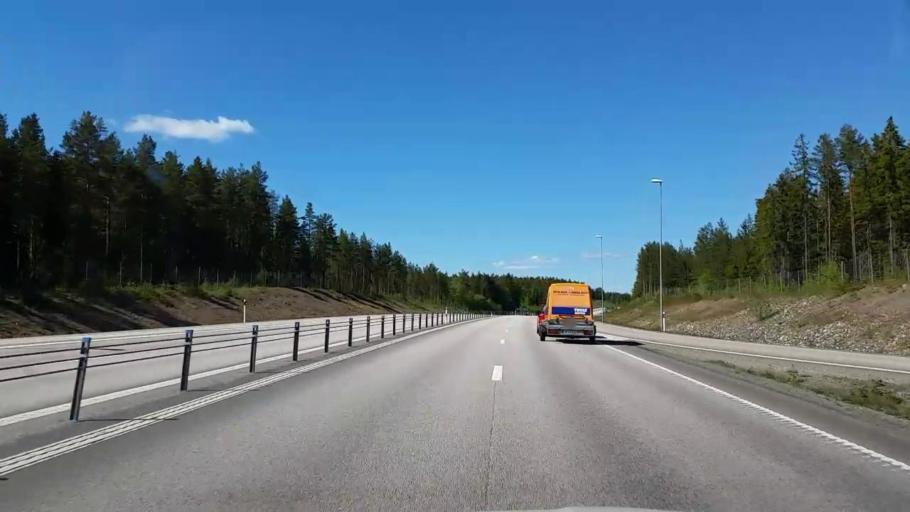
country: SE
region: Gaevleborg
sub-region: Hudiksvalls Kommun
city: Iggesund
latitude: 61.5537
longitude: 16.9750
